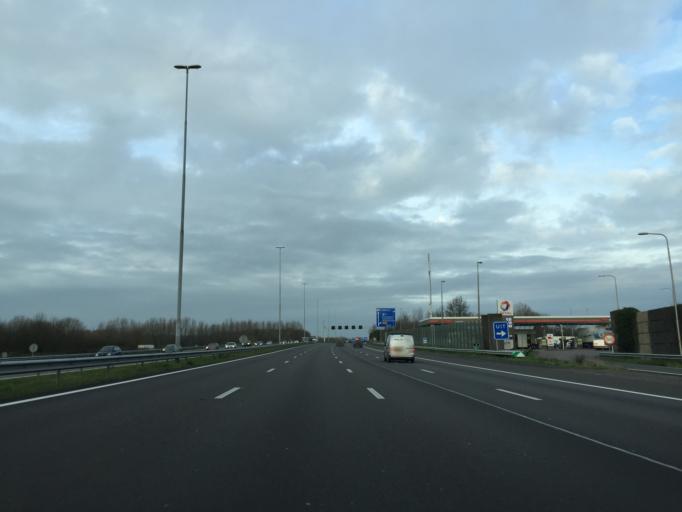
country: NL
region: Utrecht
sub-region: Gemeente Nieuwegein
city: Nieuwegein
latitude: 52.0152
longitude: 5.0688
